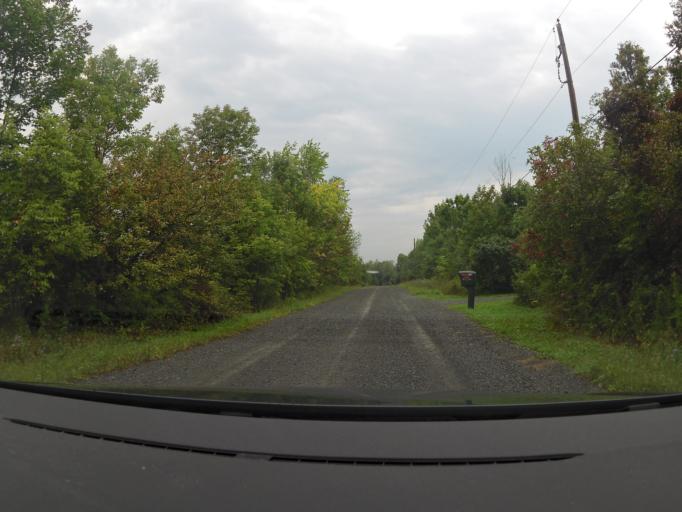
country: CA
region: Ontario
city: Carleton Place
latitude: 45.2055
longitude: -76.0716
